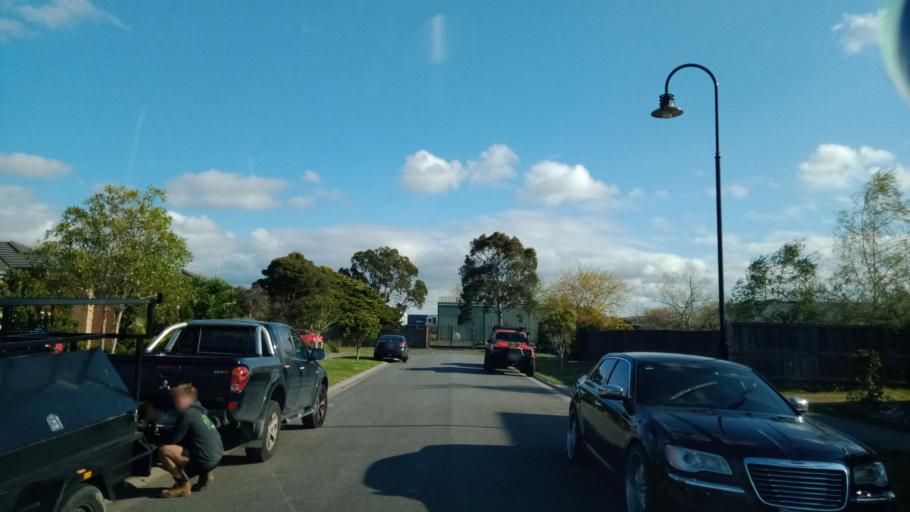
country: AU
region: Victoria
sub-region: Casey
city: Lynbrook
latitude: -38.0769
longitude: 145.2456
